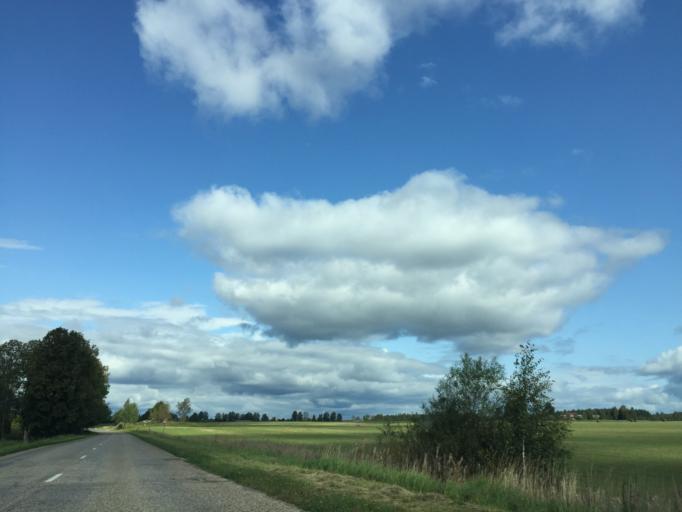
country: LV
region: Pargaujas
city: Stalbe
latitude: 57.3965
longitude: 24.9836
